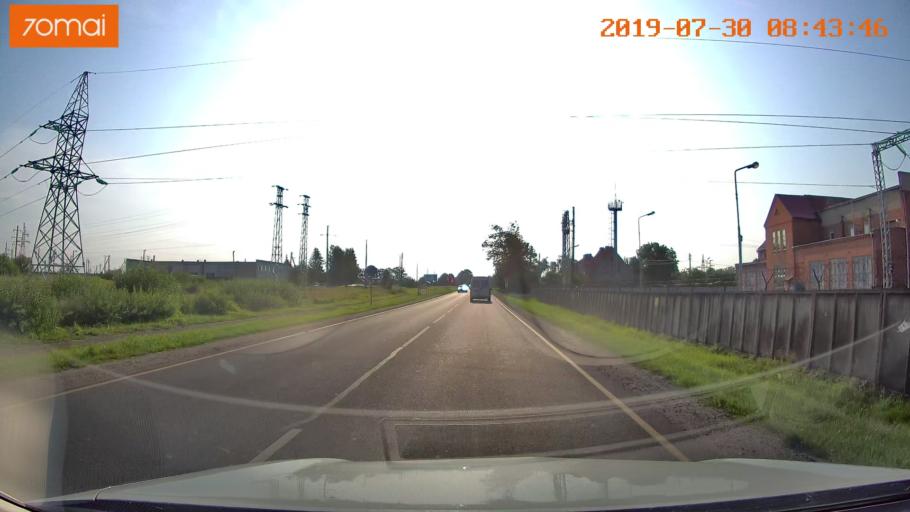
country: RU
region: Kaliningrad
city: Chernyakhovsk
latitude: 54.6268
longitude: 21.8468
